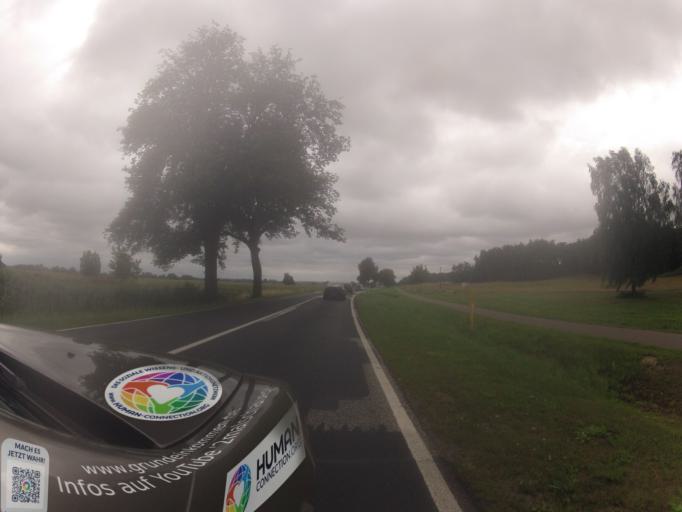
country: DE
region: Mecklenburg-Vorpommern
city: Jatznick
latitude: 53.5614
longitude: 13.9652
